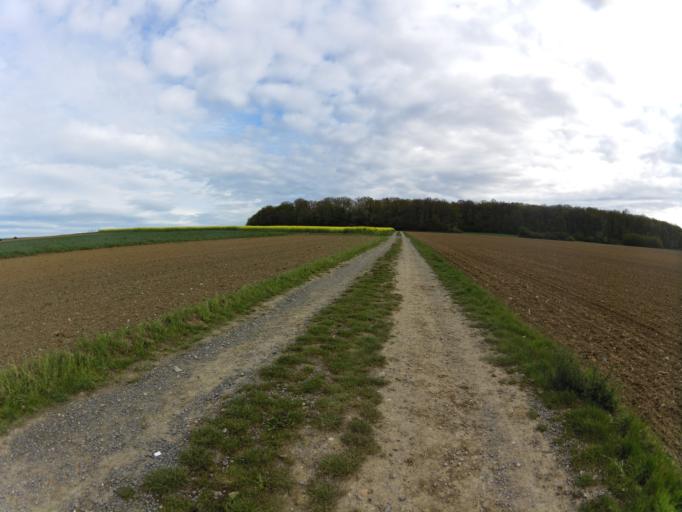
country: DE
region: Bavaria
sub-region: Regierungsbezirk Unterfranken
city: Prosselsheim
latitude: 49.8638
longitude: 10.1514
